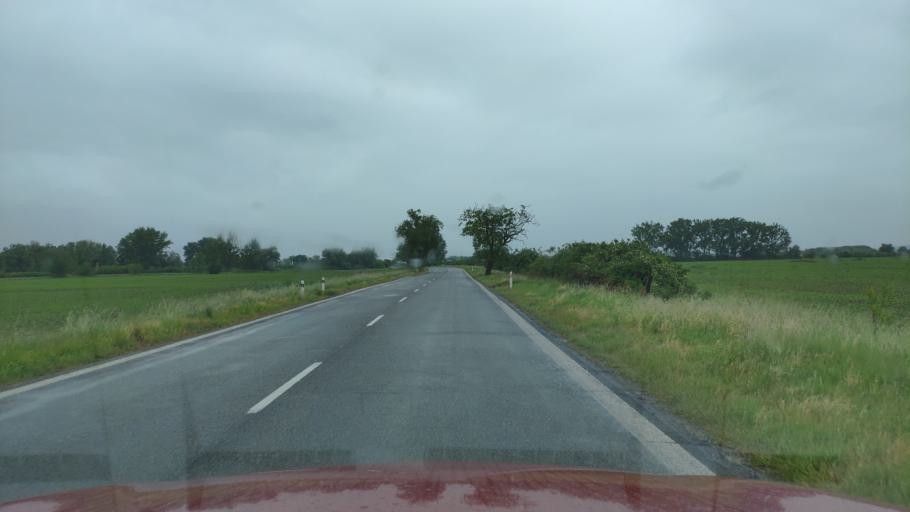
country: HU
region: Borsod-Abauj-Zemplen
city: Karcsa
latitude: 48.4086
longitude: 21.8194
